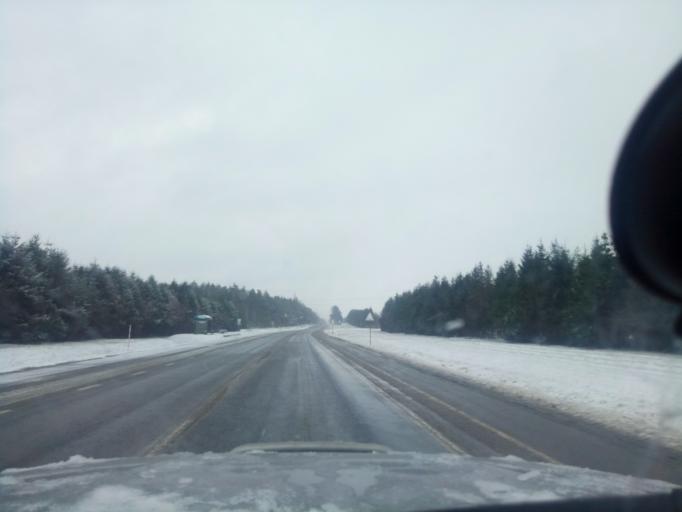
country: BY
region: Minsk
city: Haradzyeya
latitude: 53.2863
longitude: 26.5840
